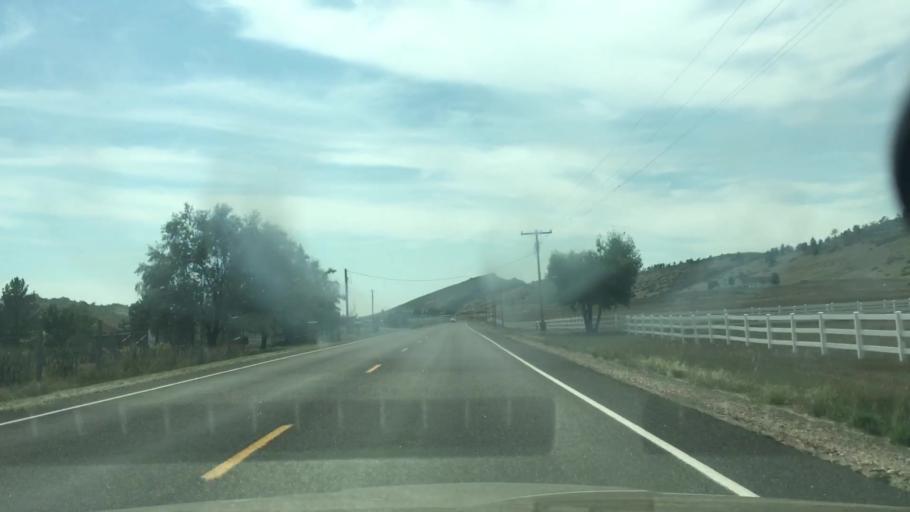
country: US
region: Colorado
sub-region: Larimer County
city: Campion
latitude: 40.3796
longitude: -105.1940
